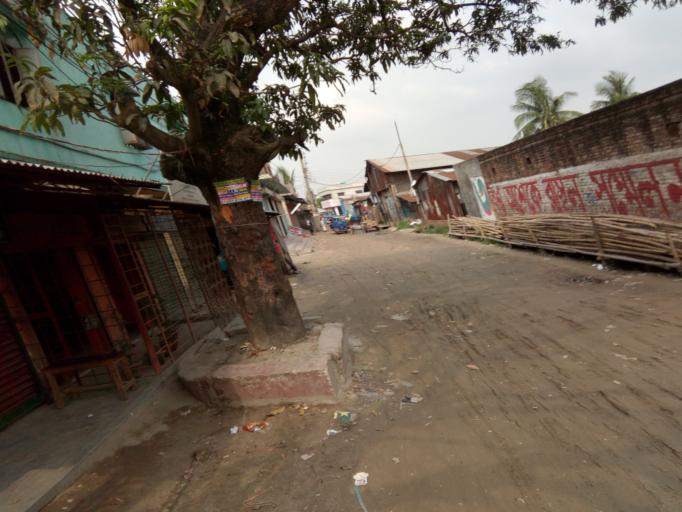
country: BD
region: Dhaka
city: Paltan
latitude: 23.7097
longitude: 90.4775
